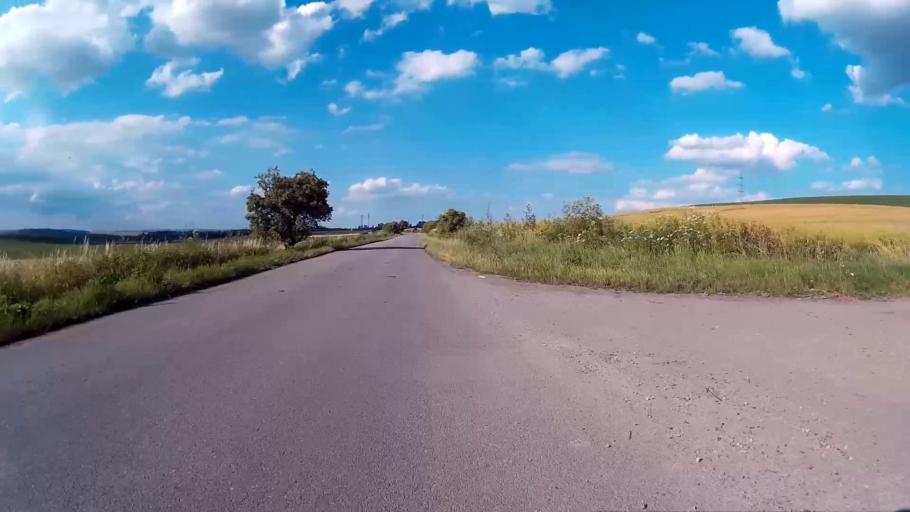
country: CZ
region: South Moravian
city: Tesany
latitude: 49.0615
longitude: 16.7840
